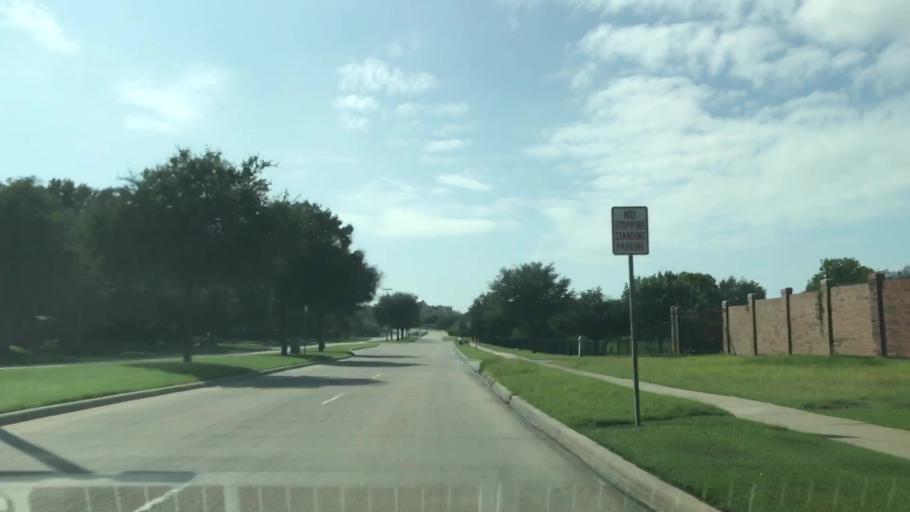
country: US
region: Texas
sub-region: Dallas County
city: Coppell
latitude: 32.9036
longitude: -96.9661
